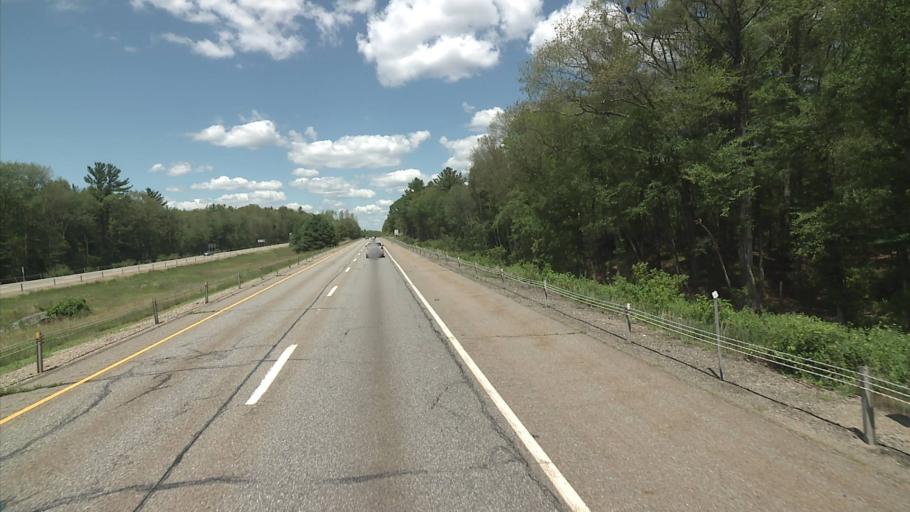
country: US
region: Massachusetts
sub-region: Worcester County
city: Webster
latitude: 42.0164
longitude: -71.8577
